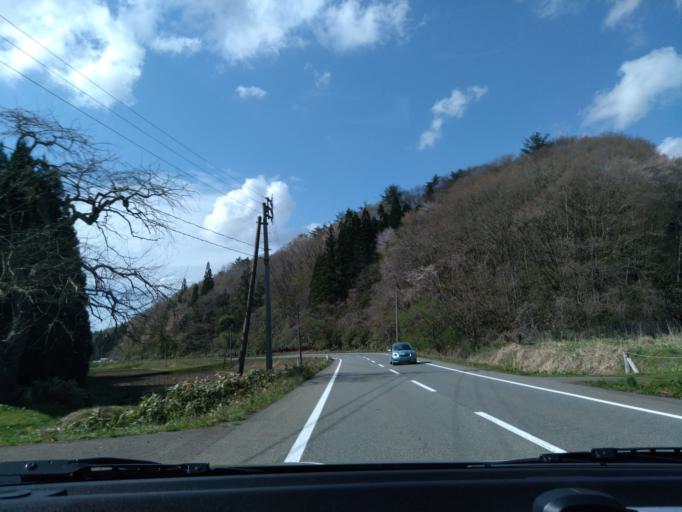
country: JP
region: Akita
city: Akita
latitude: 39.7016
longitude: 140.2171
